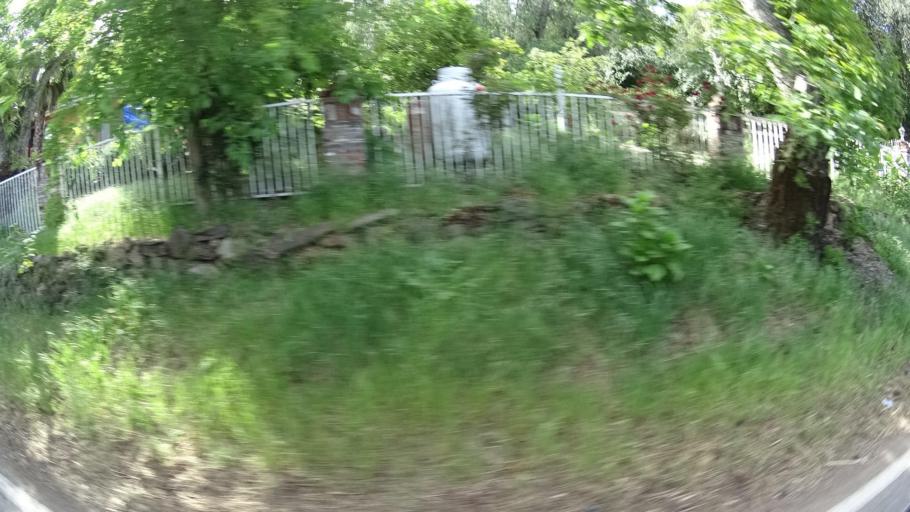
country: US
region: California
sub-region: Lake County
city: Soda Bay
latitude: 39.0051
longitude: -122.7847
